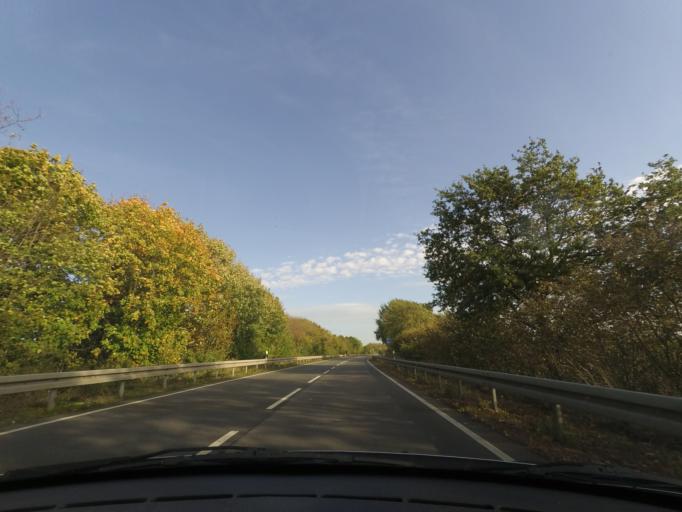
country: DE
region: North Rhine-Westphalia
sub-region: Regierungsbezirk Dusseldorf
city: Neubrueck
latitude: 51.1670
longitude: 6.6426
